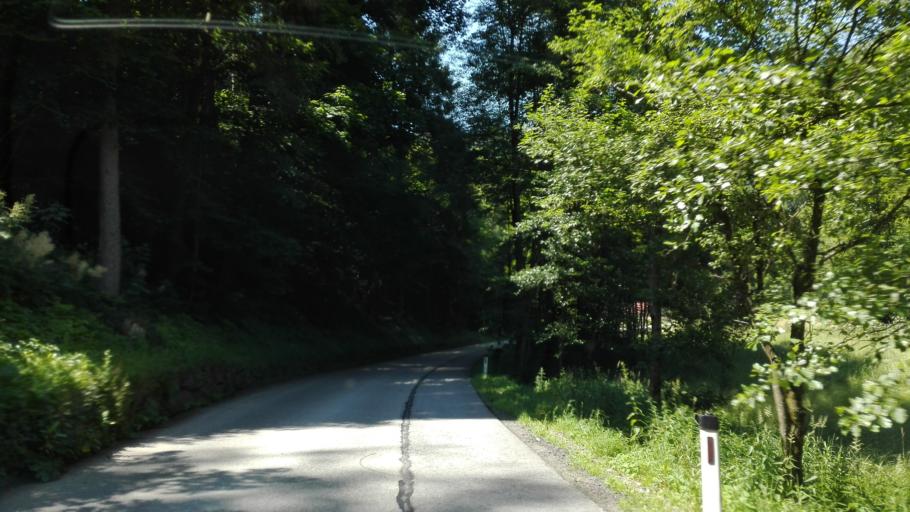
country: AT
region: Upper Austria
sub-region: Politischer Bezirk Rohrbach
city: Kleinzell im Muehlkreis
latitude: 48.3870
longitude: 13.9212
